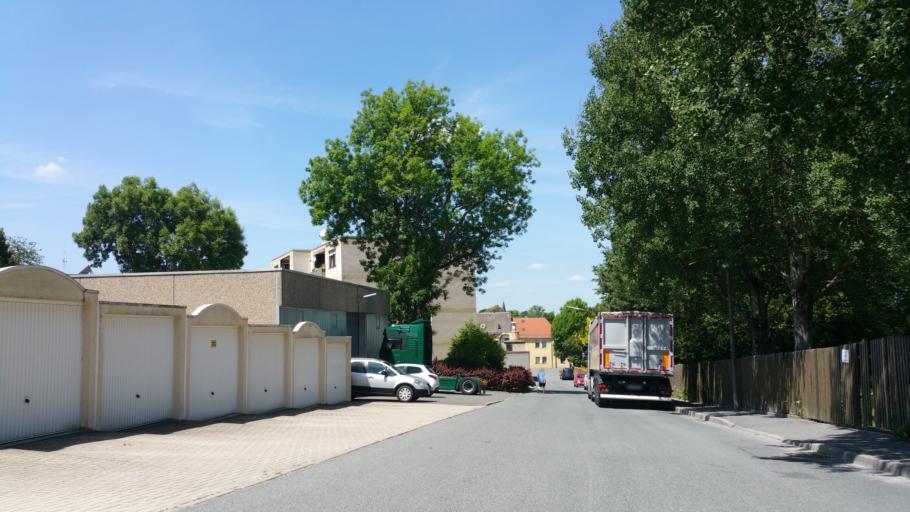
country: DE
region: Bavaria
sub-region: Upper Franconia
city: Schwarzenbach an der Saale
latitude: 50.2209
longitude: 11.9421
